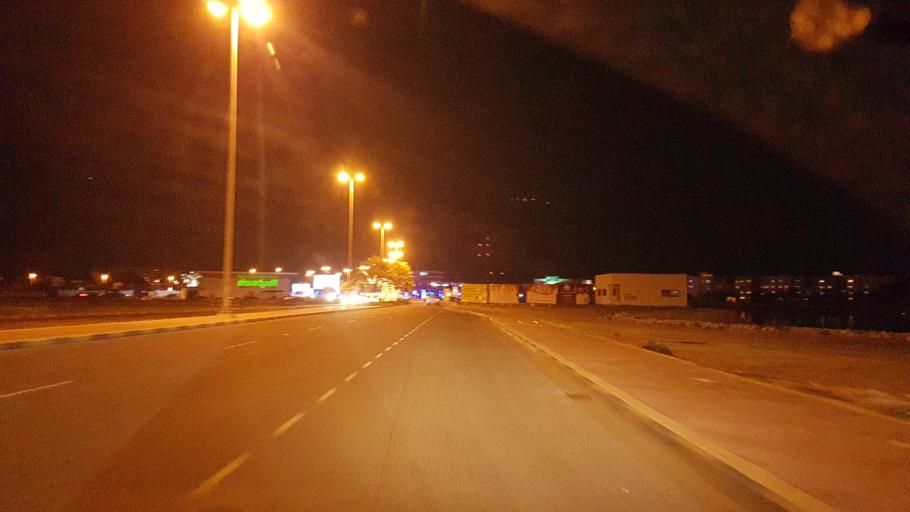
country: BH
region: Muharraq
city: Al Hadd
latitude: 26.2755
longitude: 50.6600
